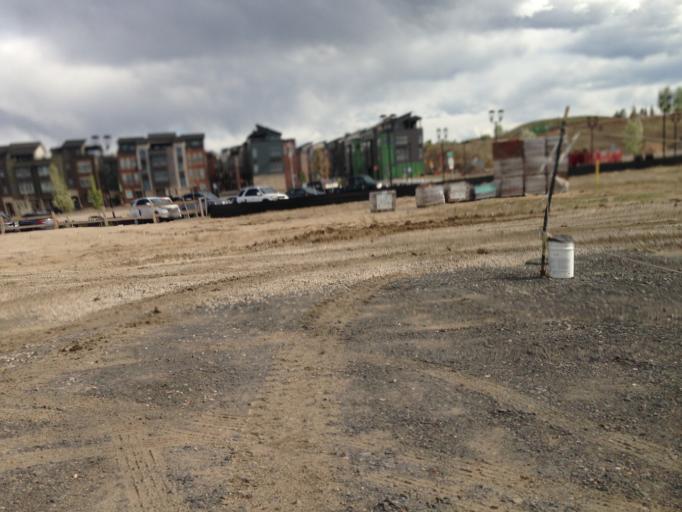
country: US
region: Colorado
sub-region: Boulder County
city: Superior
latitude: 39.9528
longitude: -105.1611
